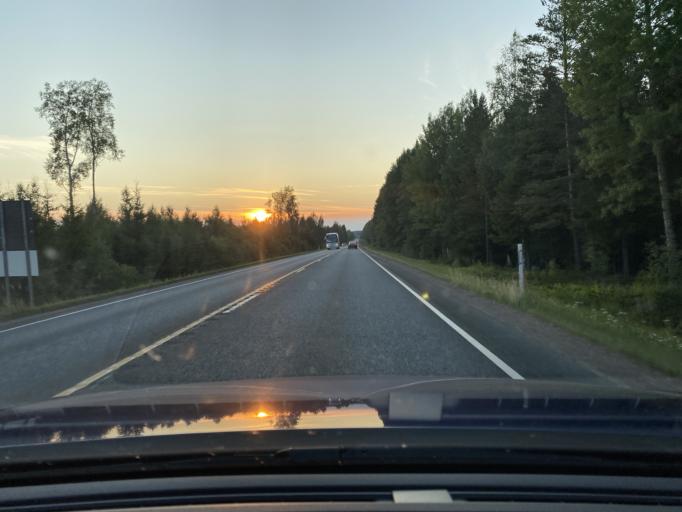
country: FI
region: Pirkanmaa
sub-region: Luoteis-Pirkanmaa
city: Ikaalinen
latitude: 61.7930
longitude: 22.9847
